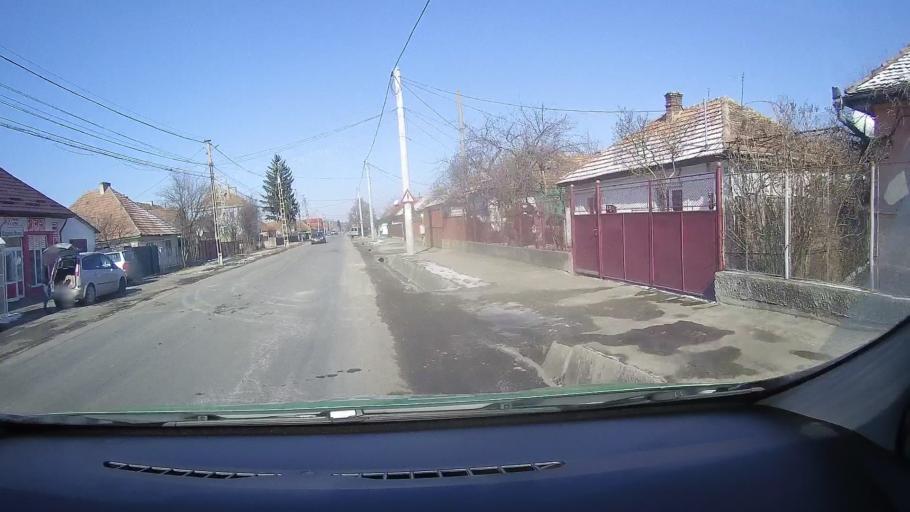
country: RO
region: Brasov
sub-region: Comuna Ungra
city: Ungra
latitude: 46.0164
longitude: 25.2753
